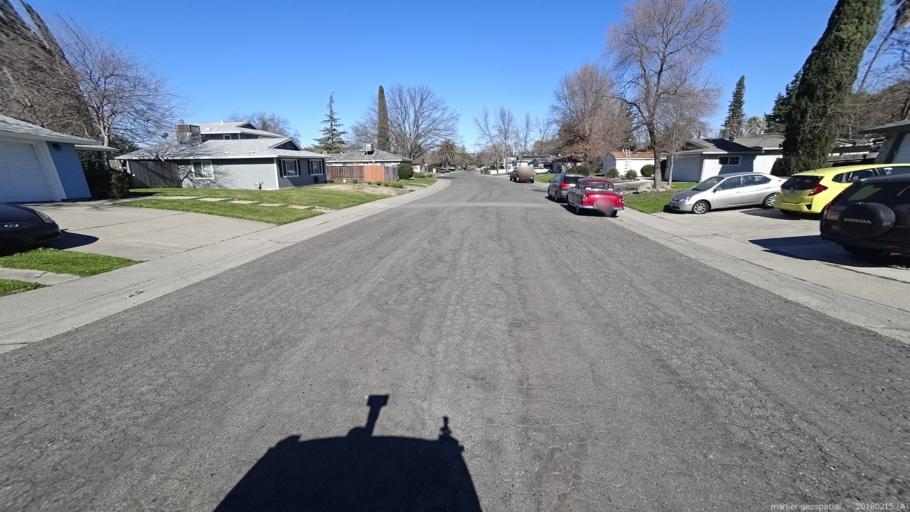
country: US
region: California
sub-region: Sacramento County
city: Foothill Farms
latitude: 38.6697
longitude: -121.3194
